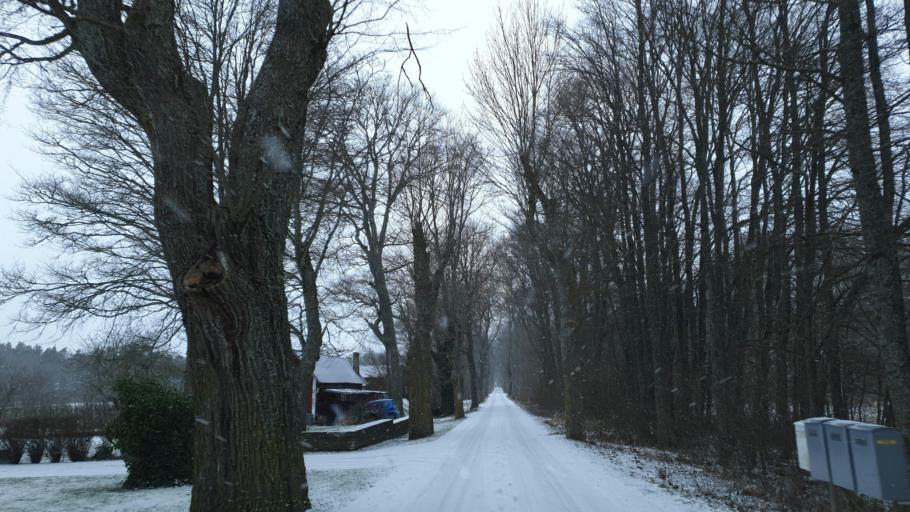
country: SE
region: Gotland
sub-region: Gotland
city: Visby
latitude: 57.5206
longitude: 18.4528
